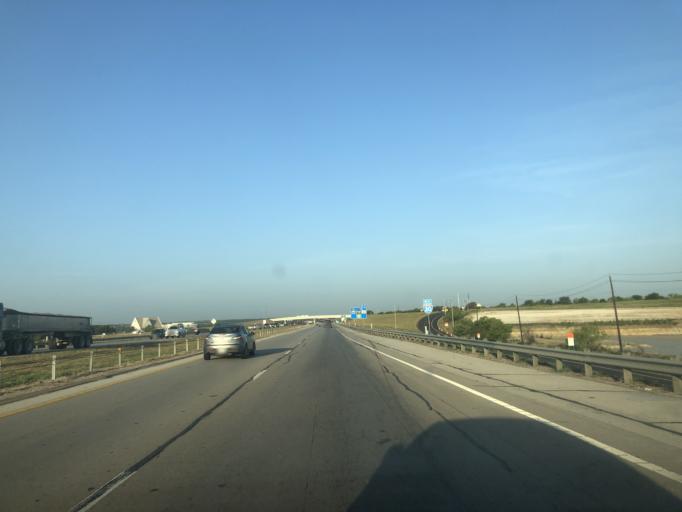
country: US
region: Texas
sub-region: Tarrant County
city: White Settlement
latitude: 32.7359
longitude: -97.4898
